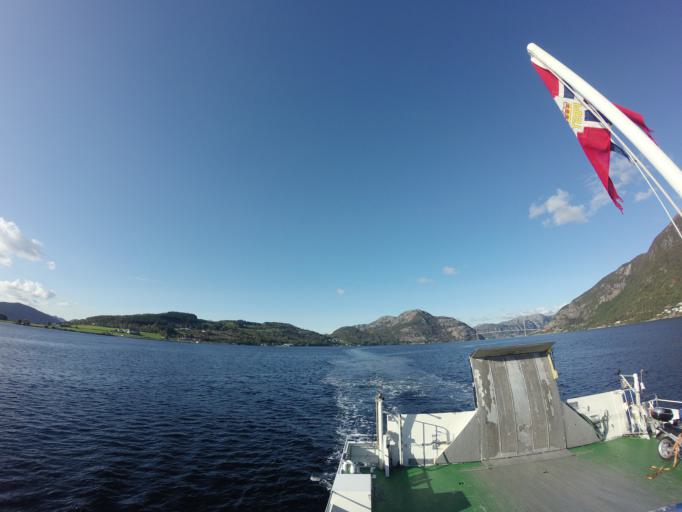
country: NO
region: Rogaland
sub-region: Forsand
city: Forsand
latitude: 58.9021
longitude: 6.0874
